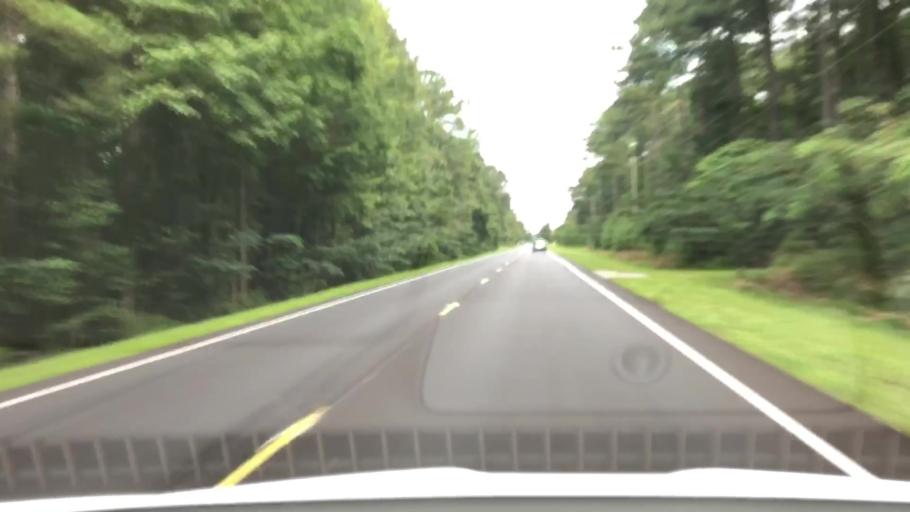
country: US
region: North Carolina
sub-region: Jones County
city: Maysville
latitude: 34.8748
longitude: -77.1999
